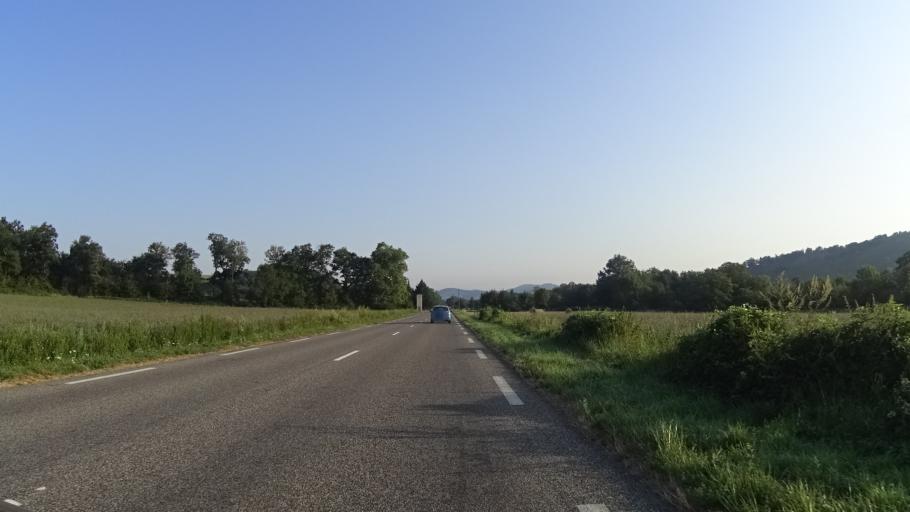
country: FR
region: Midi-Pyrenees
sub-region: Departement de l'Ariege
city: Mirepoix
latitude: 43.0683
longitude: 1.8799
